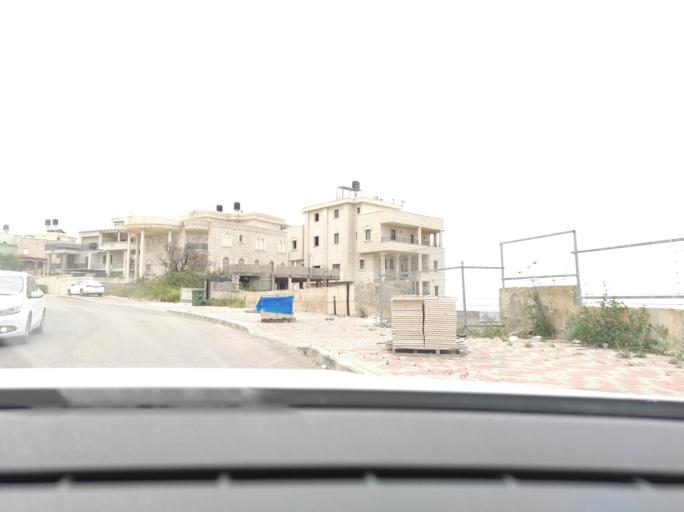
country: IL
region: Central District
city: Kafr Qasim
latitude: 32.1150
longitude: 34.9660
